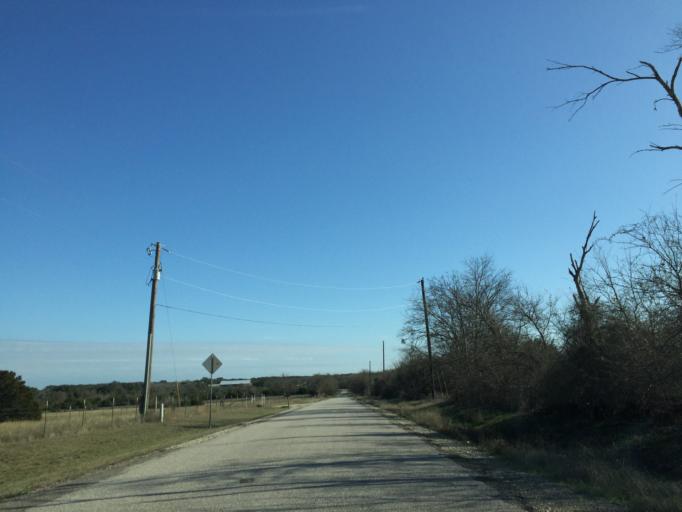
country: US
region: Texas
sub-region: Williamson County
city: Florence
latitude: 30.7763
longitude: -97.8393
